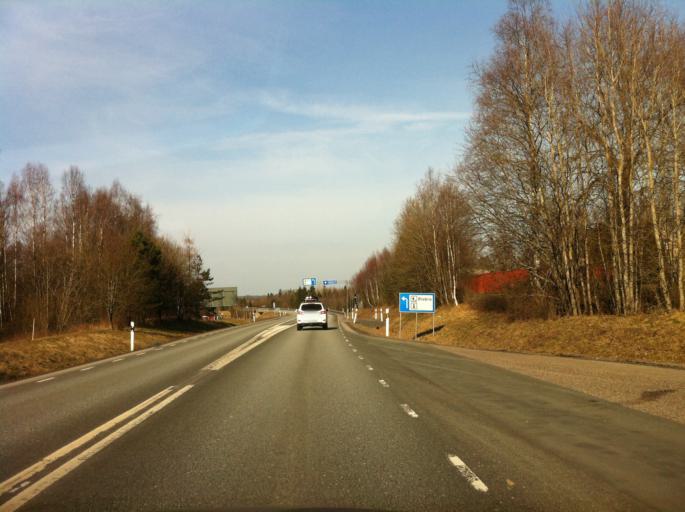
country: SE
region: Joenkoeping
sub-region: Habo Kommun
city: Habo
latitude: 57.8509
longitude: 14.0273
